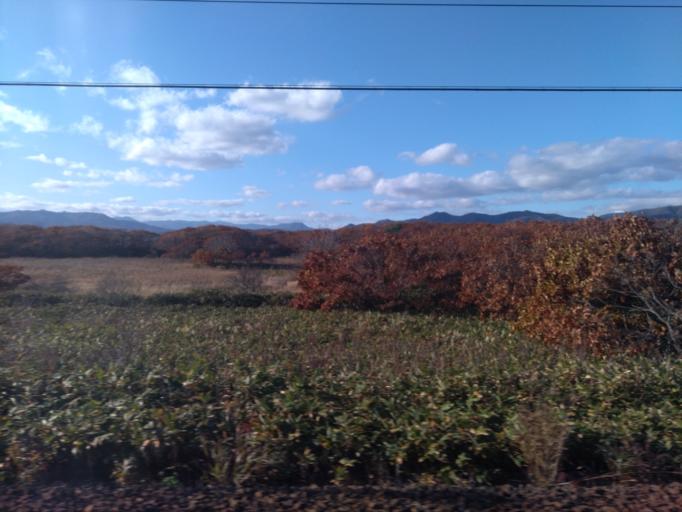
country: JP
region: Hokkaido
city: Niseko Town
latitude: 42.5372
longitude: 140.4025
